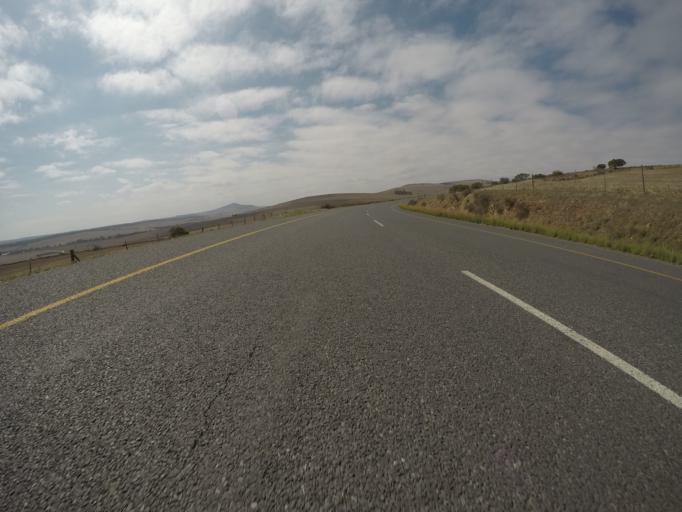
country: ZA
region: Western Cape
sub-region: City of Cape Town
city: Sunset Beach
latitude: -33.7914
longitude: 18.5712
